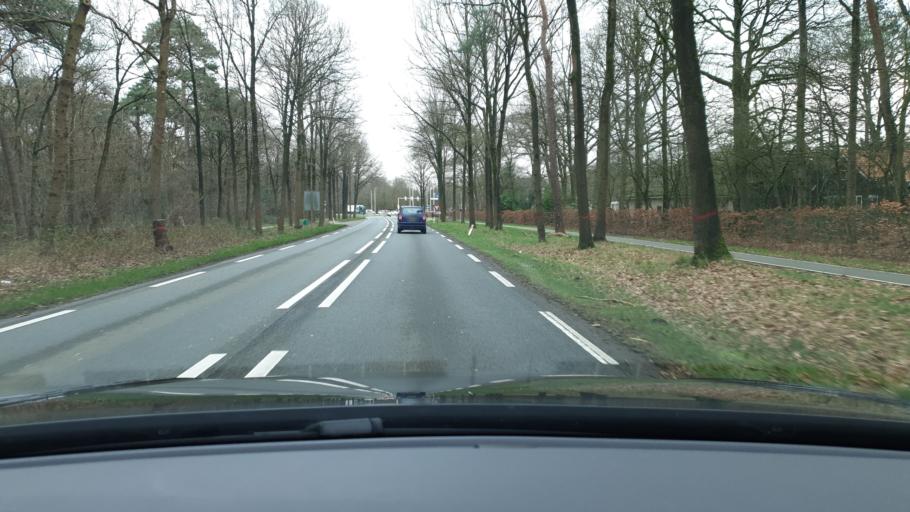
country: NL
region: North Brabant
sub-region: Gemeente Dongen
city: Dongen
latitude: 51.5823
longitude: 4.9075
